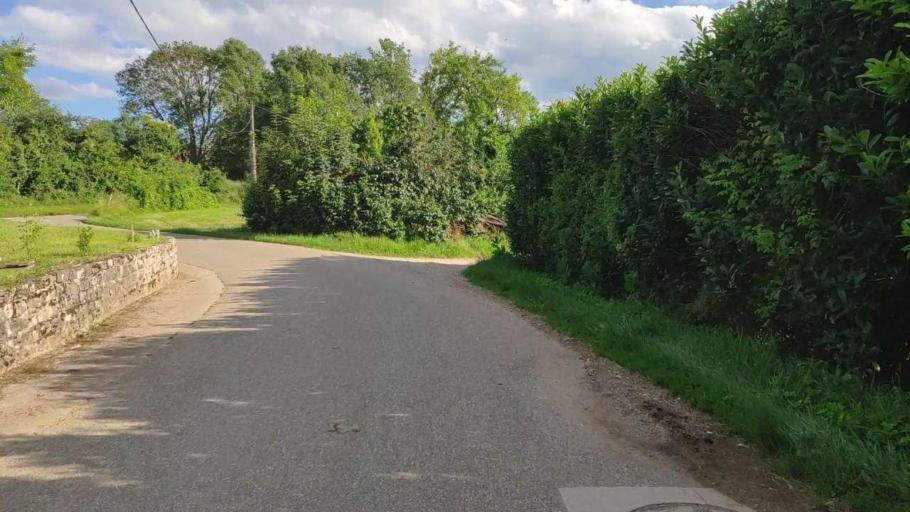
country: FR
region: Franche-Comte
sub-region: Departement du Jura
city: Bletterans
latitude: 46.7522
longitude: 5.5218
